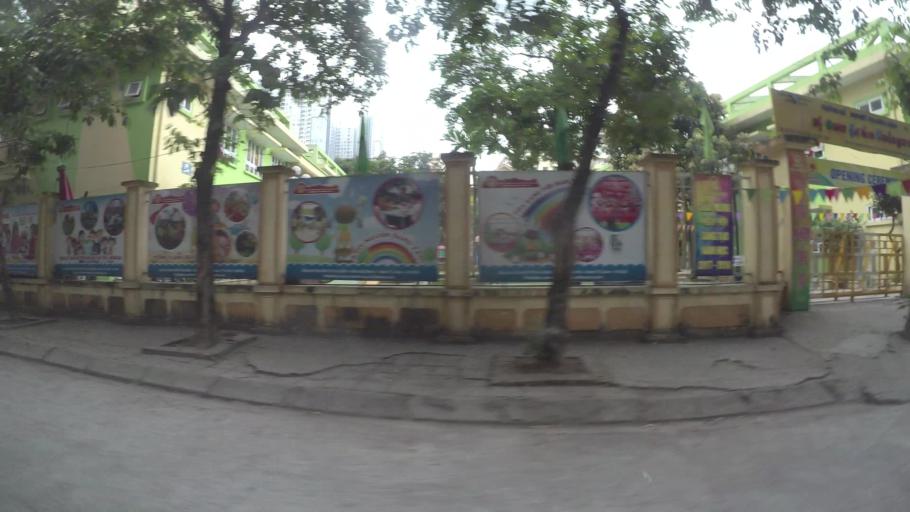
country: VN
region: Ha Noi
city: Cau Dien
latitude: 21.0319
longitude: 105.7608
